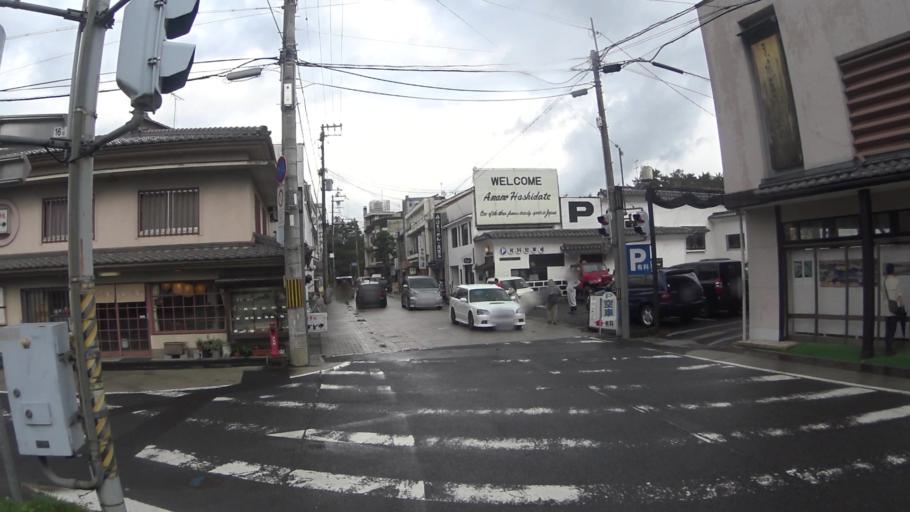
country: JP
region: Kyoto
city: Miyazu
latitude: 35.5565
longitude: 135.1837
